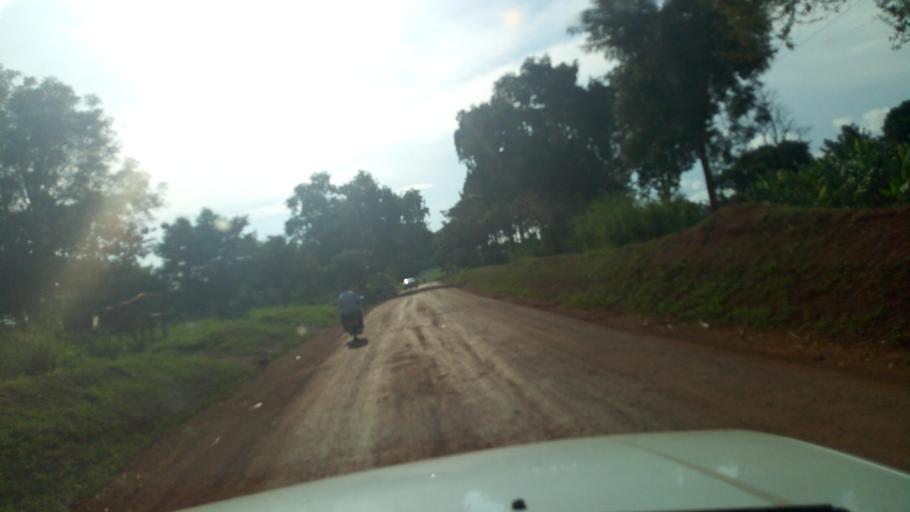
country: UG
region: Western Region
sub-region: Masindi District
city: Masindi
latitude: 1.6739
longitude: 31.6597
